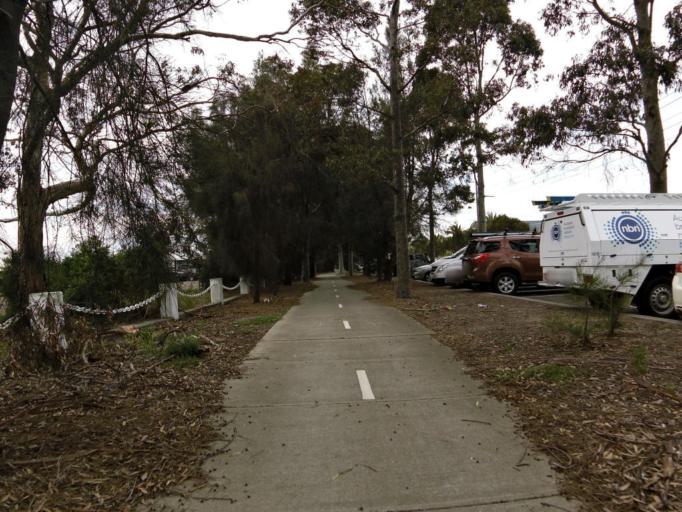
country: AU
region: Victoria
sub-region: Maribyrnong
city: Yarraville
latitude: -37.8253
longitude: 144.9050
